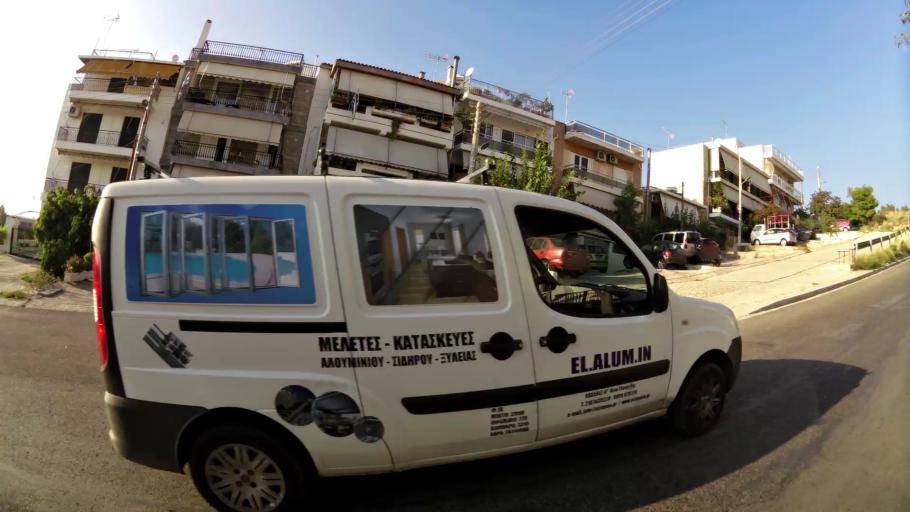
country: GR
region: Attica
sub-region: Nomarchia Athinas
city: Argyroupoli
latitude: 37.8965
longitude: 23.7602
